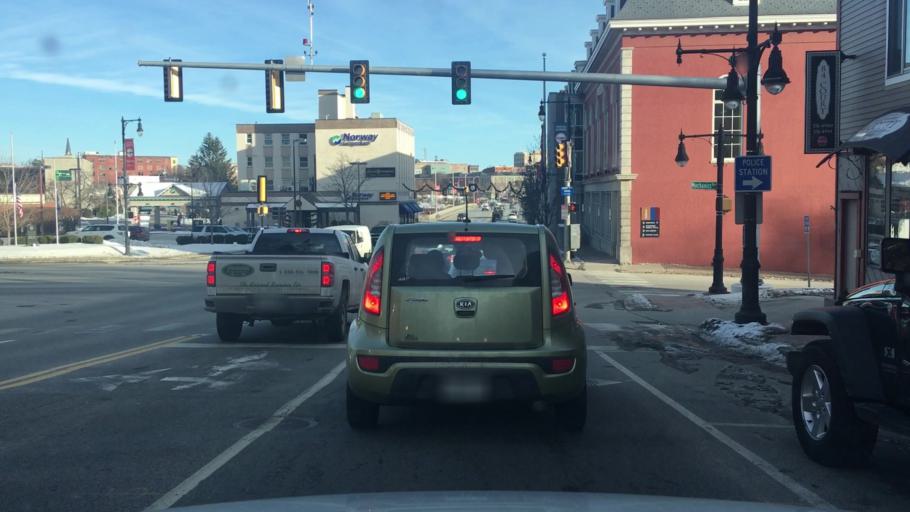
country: US
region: Maine
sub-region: Androscoggin County
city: Auburn
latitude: 44.0975
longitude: -70.2266
